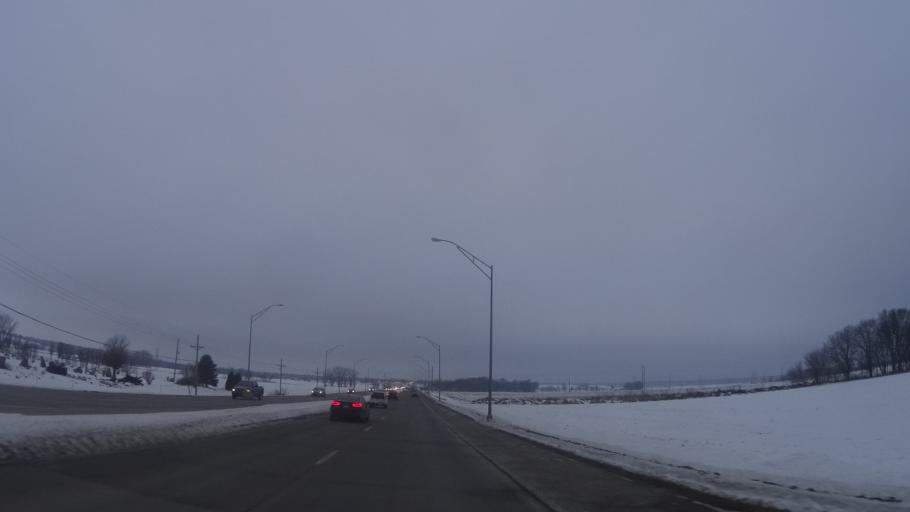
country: US
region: Nebraska
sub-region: Sarpy County
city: Offutt Air Force Base
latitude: 41.1620
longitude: -95.9703
